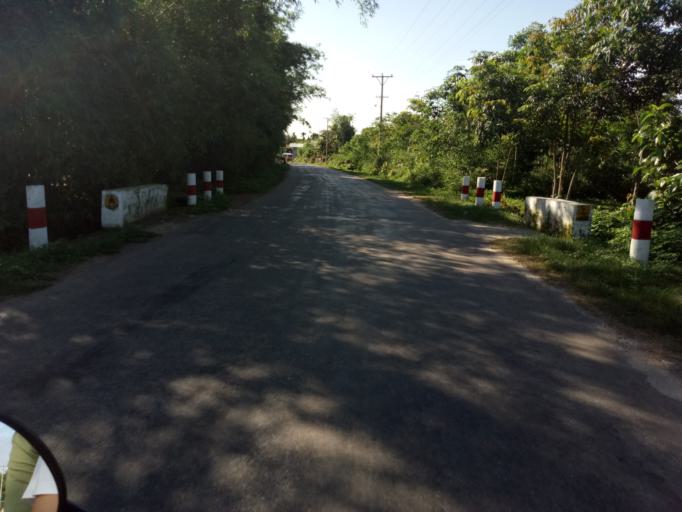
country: MM
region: Mon
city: Mawlamyine
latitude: 16.3656
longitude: 97.5577
